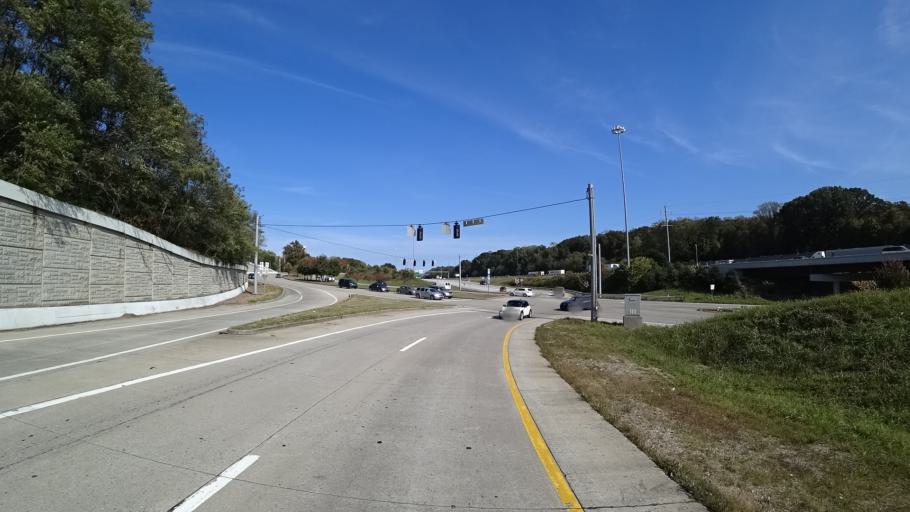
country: US
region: Tennessee
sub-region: Knox County
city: Knoxville
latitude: 35.9432
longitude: -84.0018
